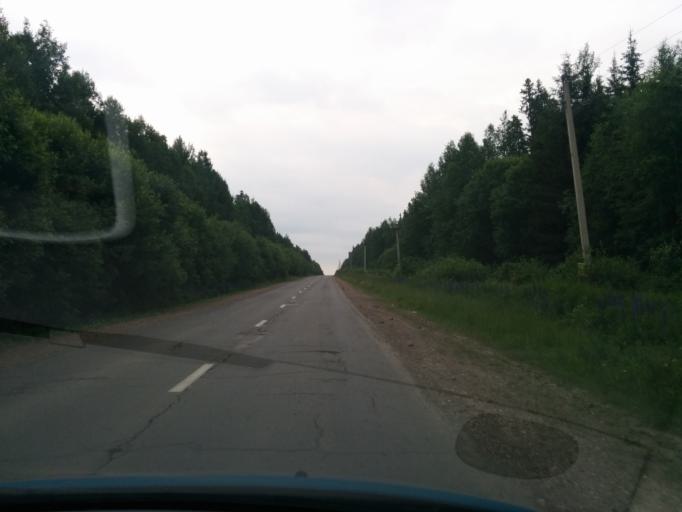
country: RU
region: Perm
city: Perm
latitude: 58.1967
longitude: 56.2139
